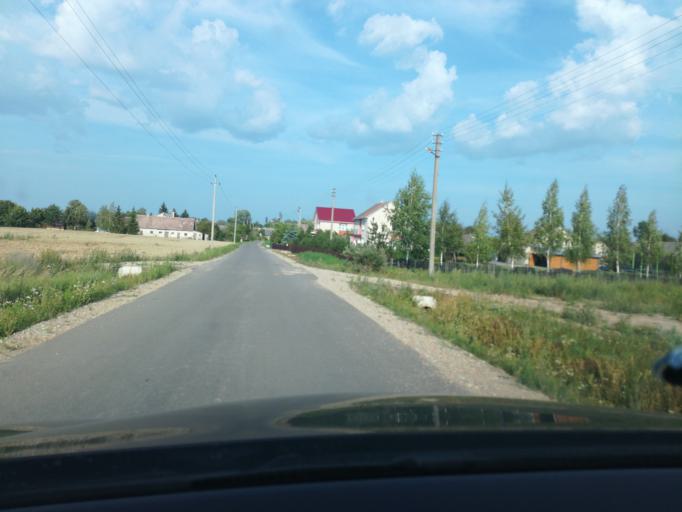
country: LT
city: Simnas
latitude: 54.3852
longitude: 23.6807
